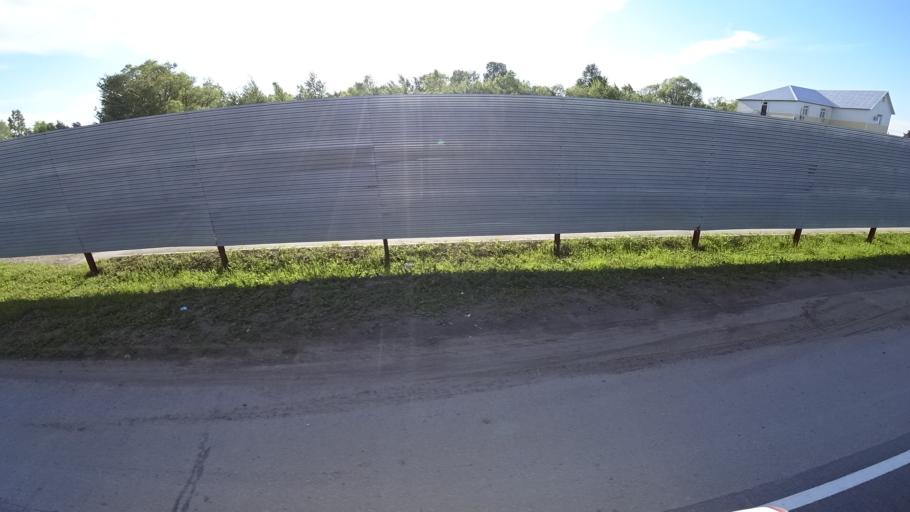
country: RU
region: Khabarovsk Krai
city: Khor
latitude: 47.8513
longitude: 134.9606
